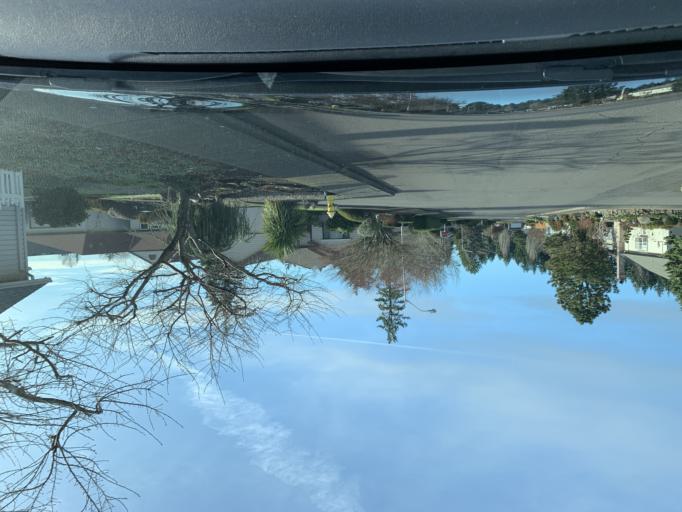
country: US
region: Washington
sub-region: Clark County
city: Mill Plain
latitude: 45.5986
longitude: -122.5145
